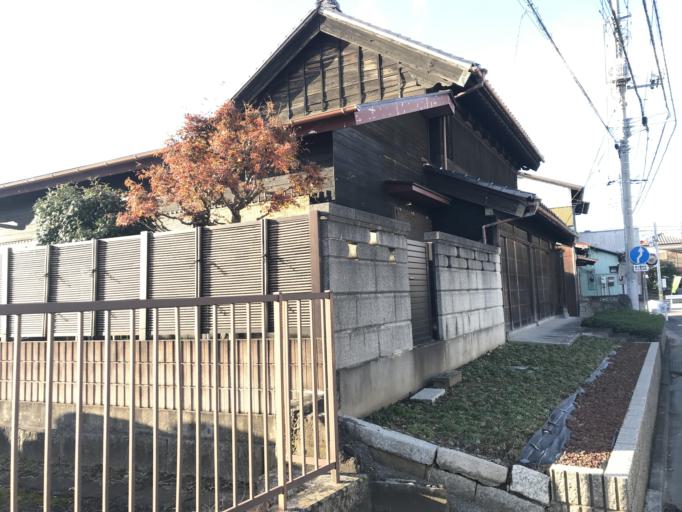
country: JP
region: Ibaraki
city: Naka
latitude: 36.0853
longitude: 140.1952
